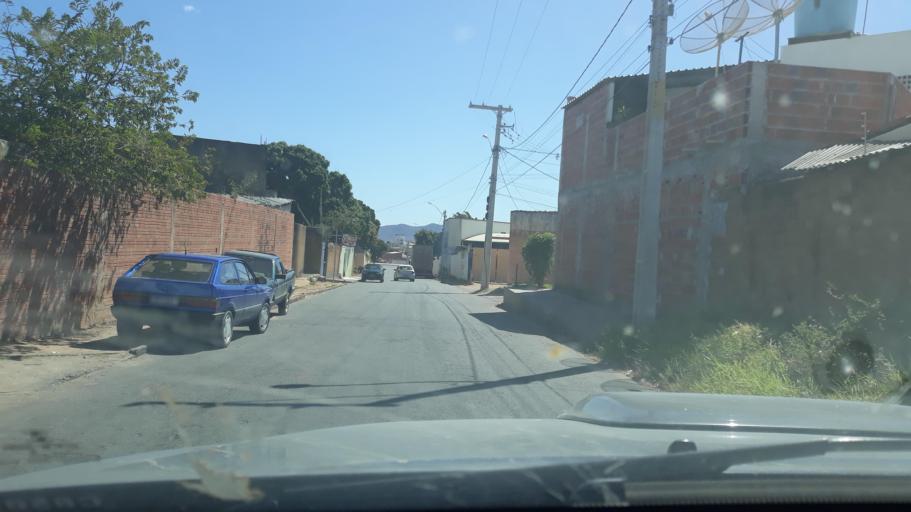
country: BR
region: Bahia
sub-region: Guanambi
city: Guanambi
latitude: -14.2125
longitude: -42.7888
